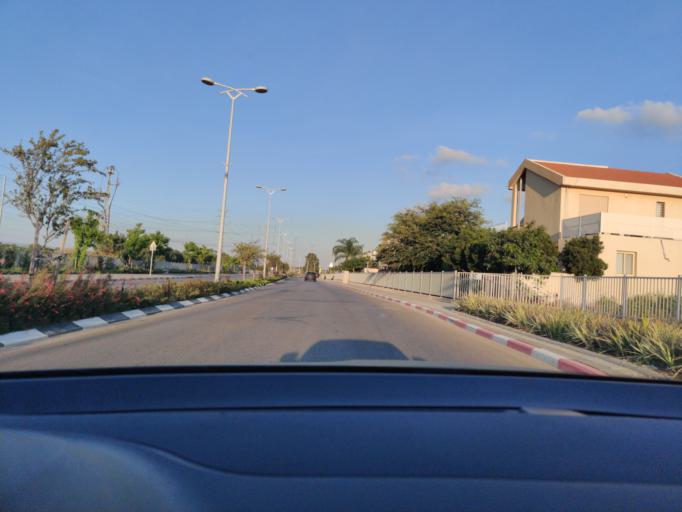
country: IL
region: Central District
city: Elyakhin
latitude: 32.4375
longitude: 34.9410
